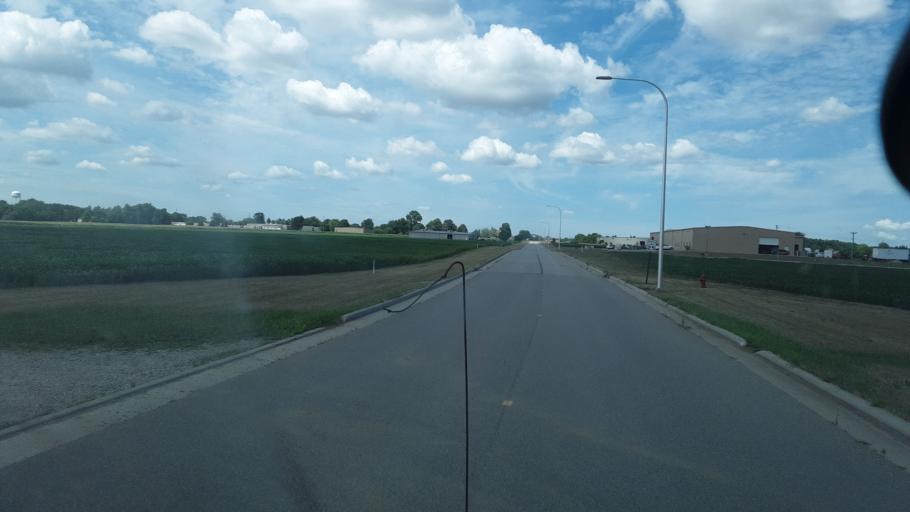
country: US
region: Ohio
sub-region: Defiance County
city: Hicksville
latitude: 41.3070
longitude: -84.7575
